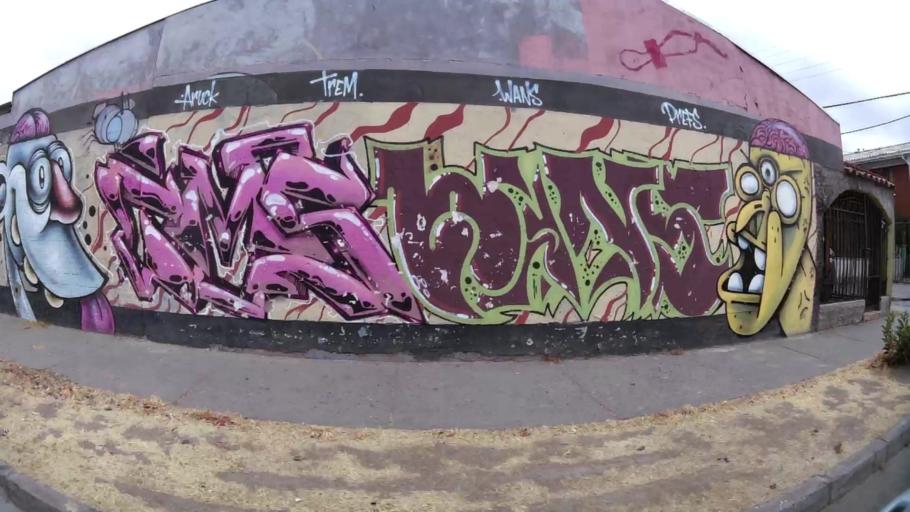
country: CL
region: O'Higgins
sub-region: Provincia de Cachapoal
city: Rancagua
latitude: -34.1613
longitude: -70.7400
